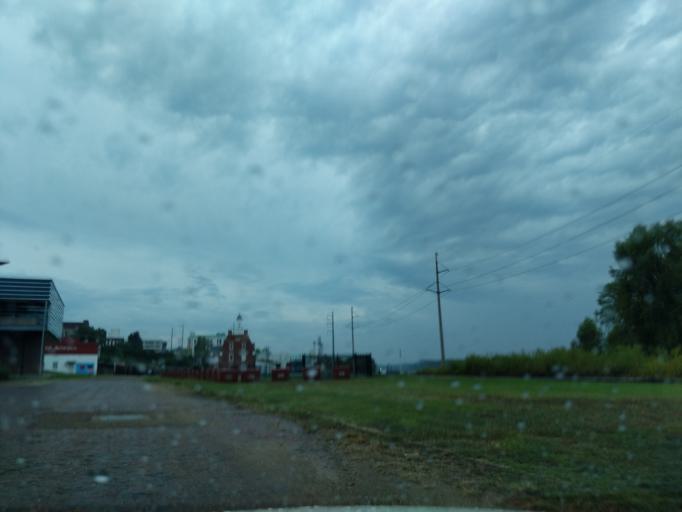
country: US
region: Mississippi
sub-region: Warren County
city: Vicksburg
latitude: 32.3542
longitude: -90.8821
